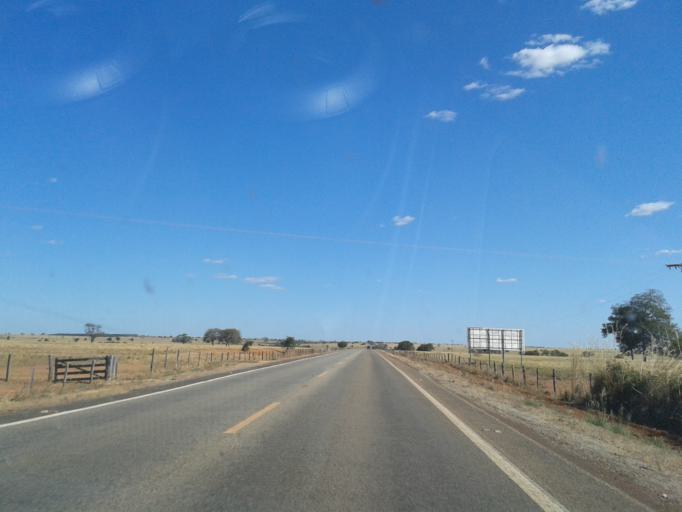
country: BR
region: Goias
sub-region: Mozarlandia
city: Mozarlandia
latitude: -14.3308
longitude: -50.4142
